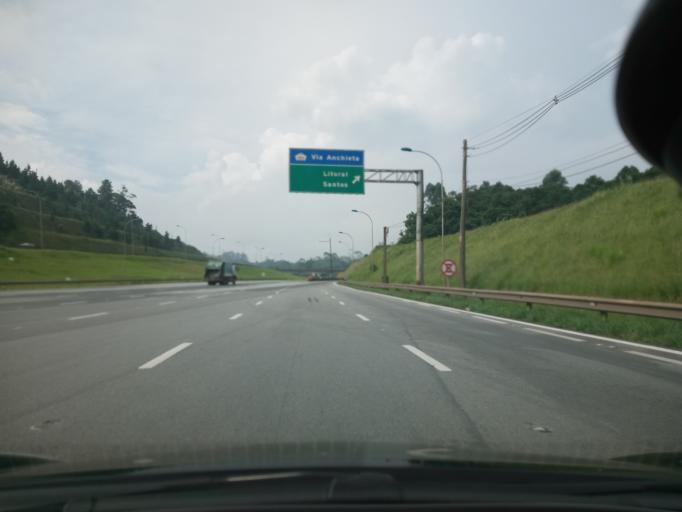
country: BR
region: Sao Paulo
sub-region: Sao Bernardo Do Campo
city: Sao Bernardo do Campo
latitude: -23.7550
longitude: -46.5401
